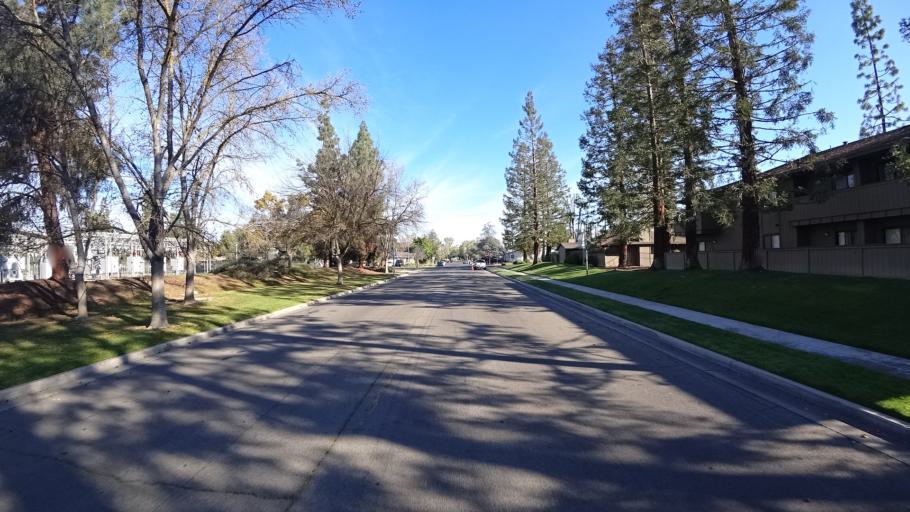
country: US
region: California
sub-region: Fresno County
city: West Park
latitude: 36.8218
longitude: -119.8580
